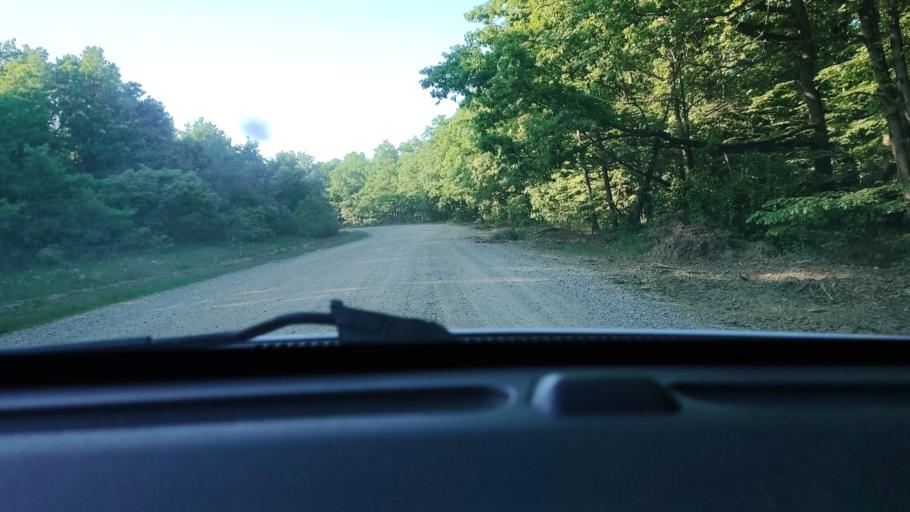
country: RU
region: Krasnodarskiy
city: Novodmitriyevskaya
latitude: 44.7170
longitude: 38.9916
